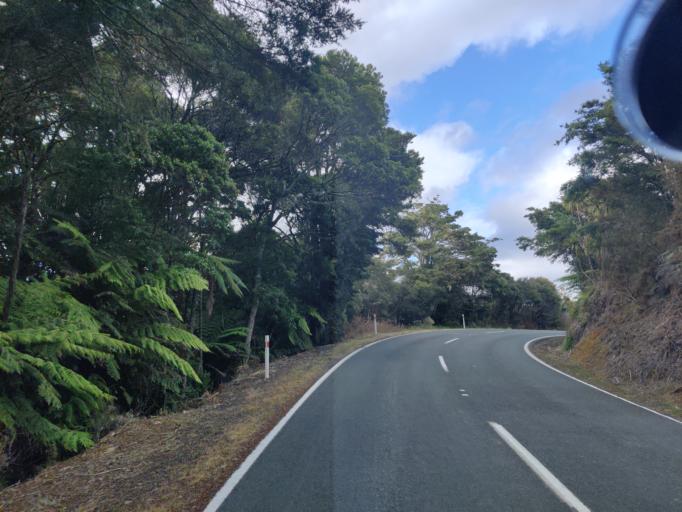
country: NZ
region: Northland
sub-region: Whangarei
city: Ngunguru
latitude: -35.5826
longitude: 174.4248
